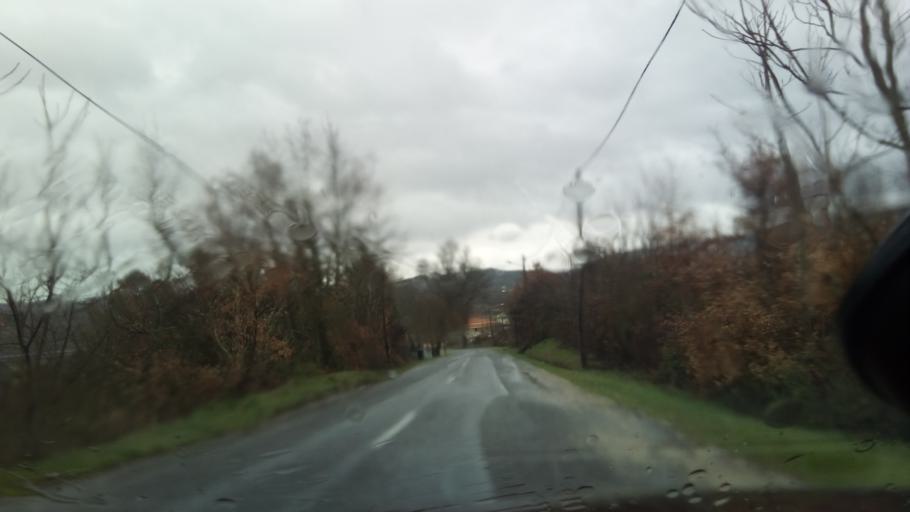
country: PT
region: Guarda
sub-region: Celorico da Beira
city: Celorico da Beira
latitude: 40.6303
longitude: -7.4399
